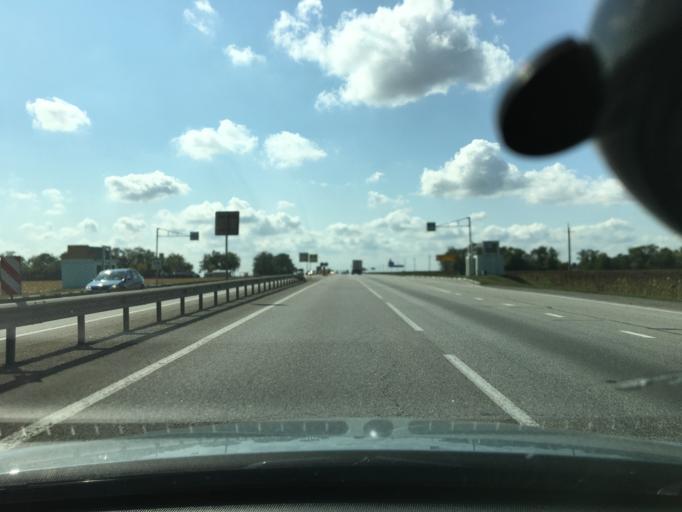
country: RU
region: Krasnodarskiy
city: Krasnoye
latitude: 46.7556
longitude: 39.6604
